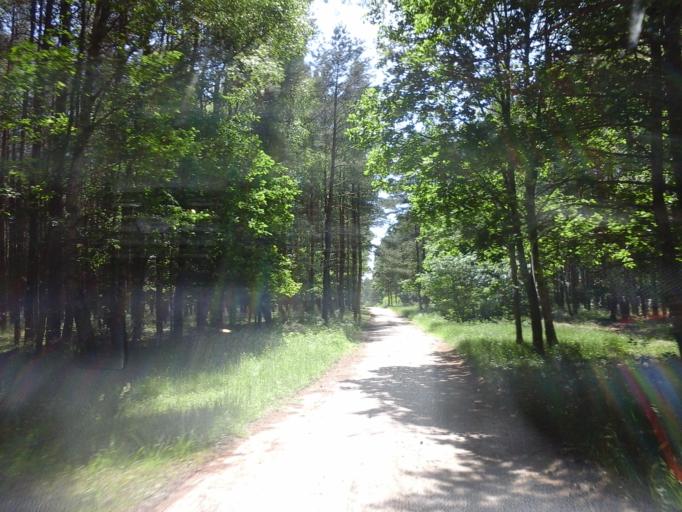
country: PL
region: West Pomeranian Voivodeship
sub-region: Powiat choszczenski
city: Drawno
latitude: 53.1305
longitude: 15.8380
